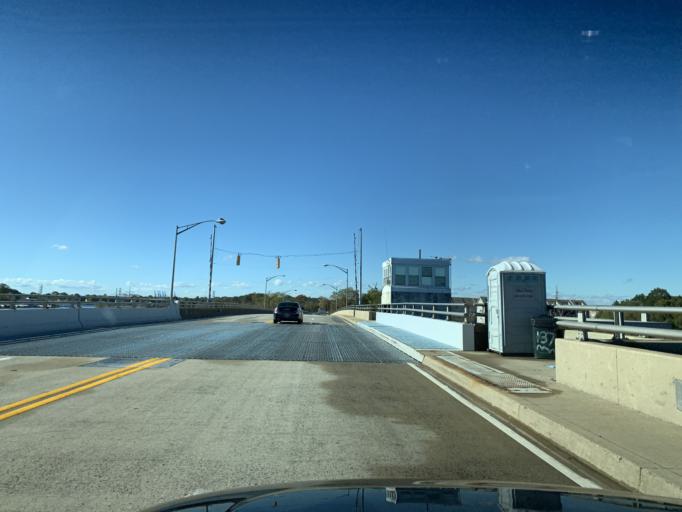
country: US
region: Maryland
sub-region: Baltimore County
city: Dundalk
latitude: 39.2482
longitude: -76.4912
